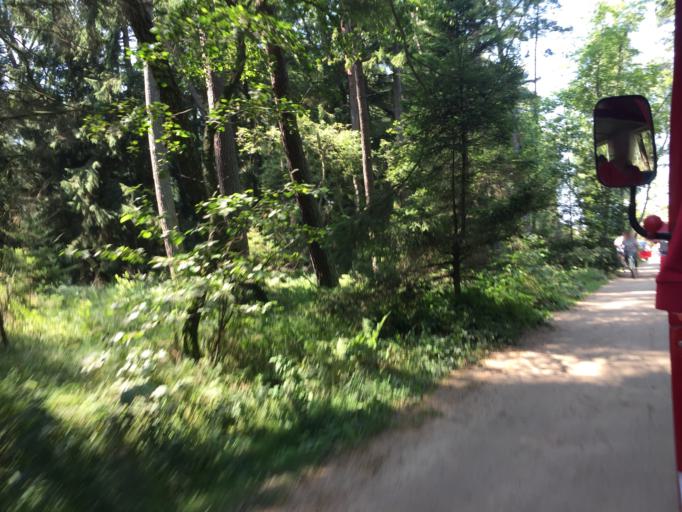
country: PL
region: Pomeranian Voivodeship
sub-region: Powiat leborski
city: Leba
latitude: 54.7486
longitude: 17.4415
